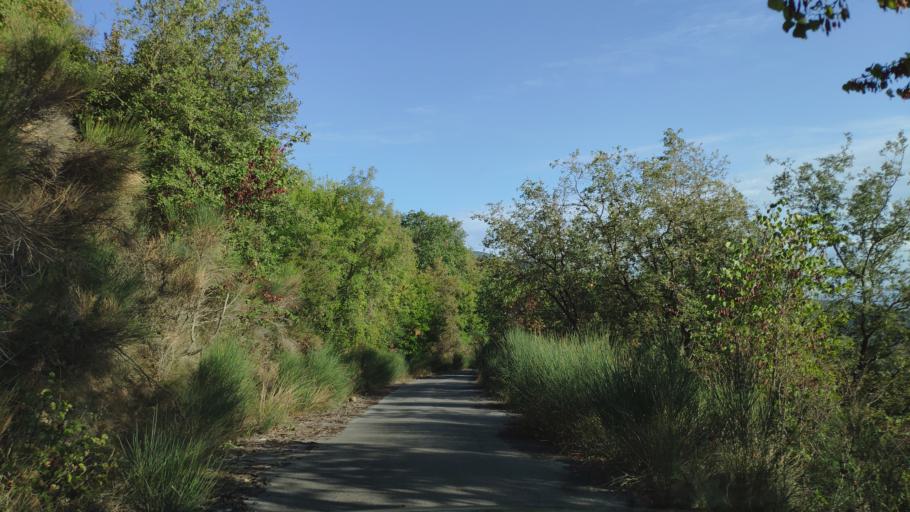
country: GR
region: Peloponnese
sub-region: Nomos Arkadias
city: Dimitsana
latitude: 37.5502
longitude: 22.0439
